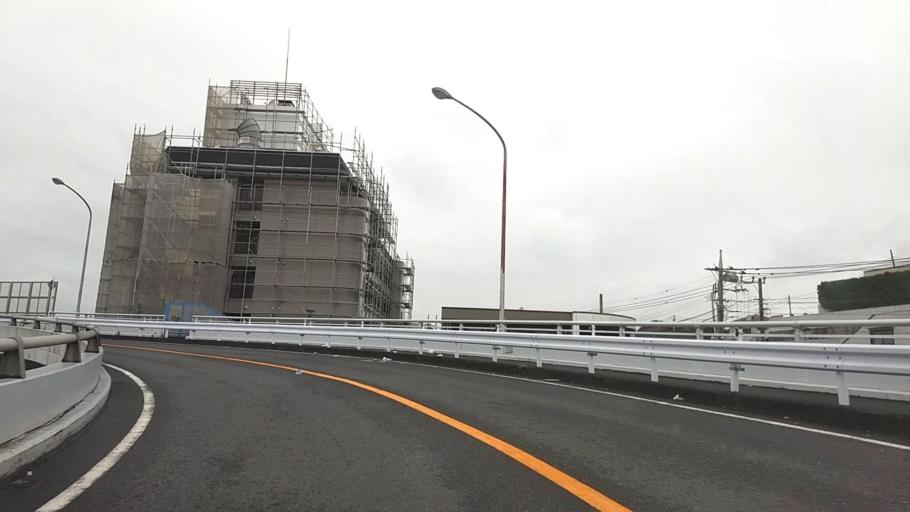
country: JP
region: Kanagawa
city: Fujisawa
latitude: 35.3883
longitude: 139.5348
